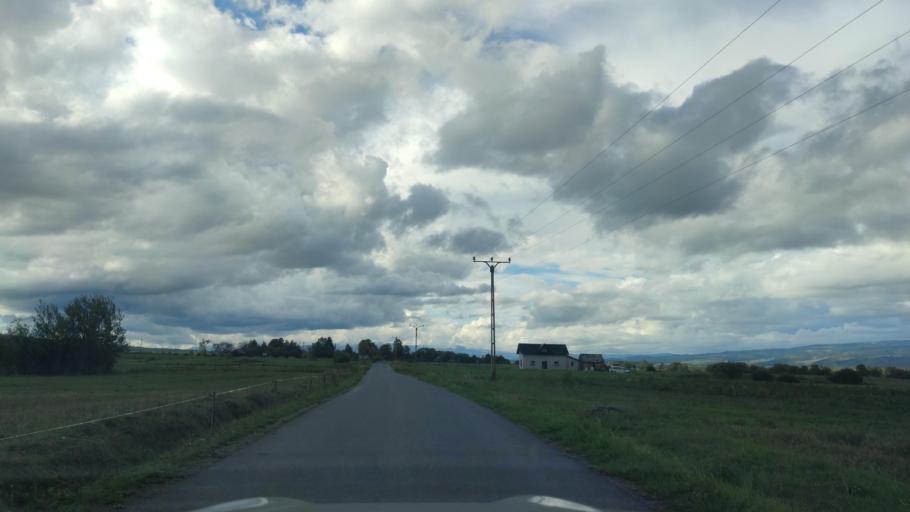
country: RO
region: Harghita
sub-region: Comuna Remetea
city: Remetea
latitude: 46.8058
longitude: 25.4399
